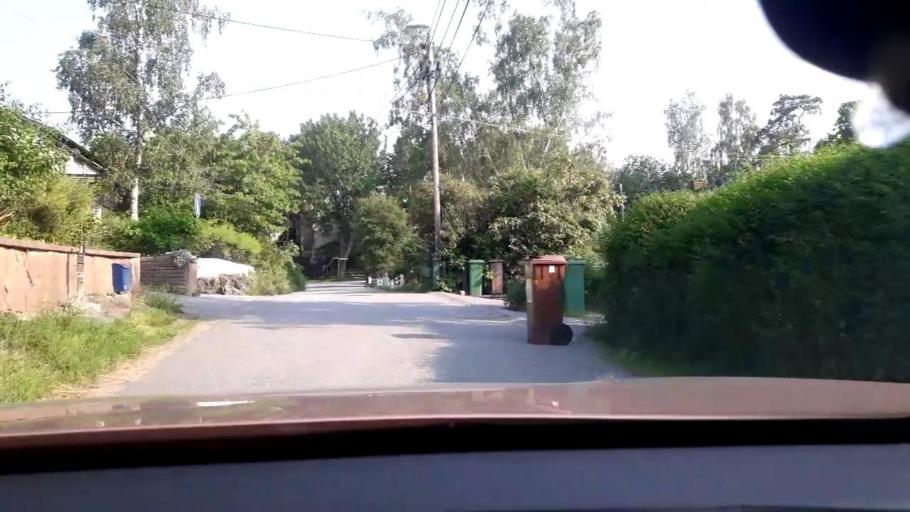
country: SE
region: Stockholm
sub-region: Lidingo
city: Brevik
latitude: 59.3214
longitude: 18.2100
